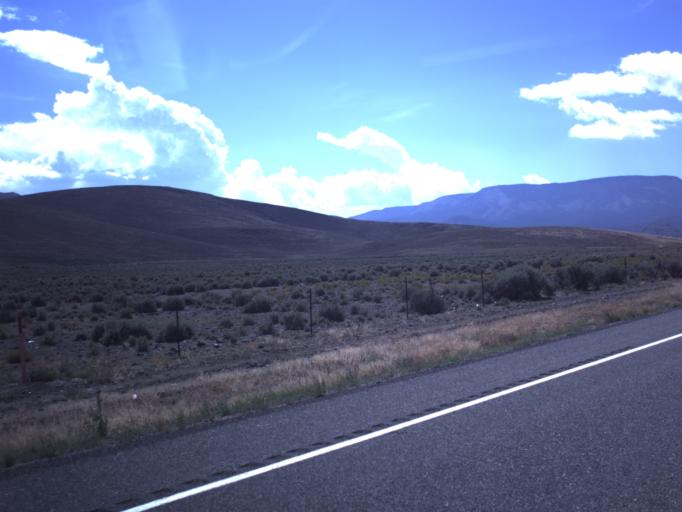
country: US
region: Utah
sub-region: Piute County
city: Junction
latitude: 38.2675
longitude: -112.2221
